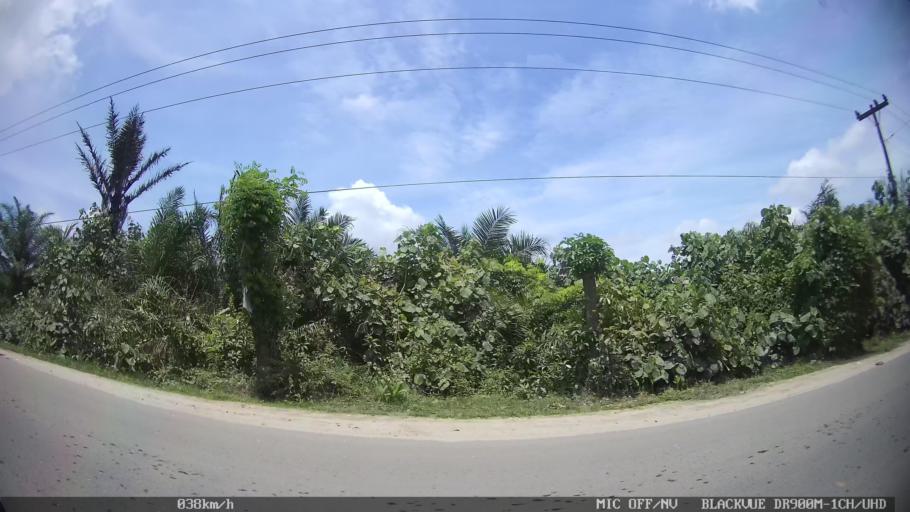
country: ID
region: North Sumatra
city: Perbaungan
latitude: 3.5383
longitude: 98.8824
